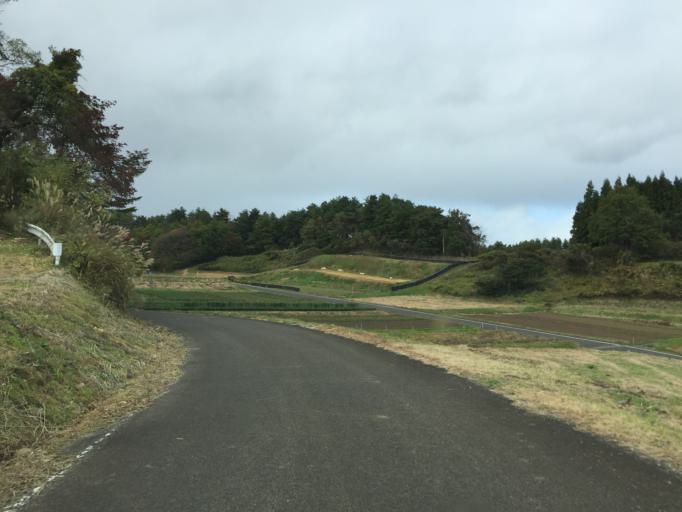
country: JP
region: Fukushima
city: Fukushima-shi
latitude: 37.6992
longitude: 140.3861
